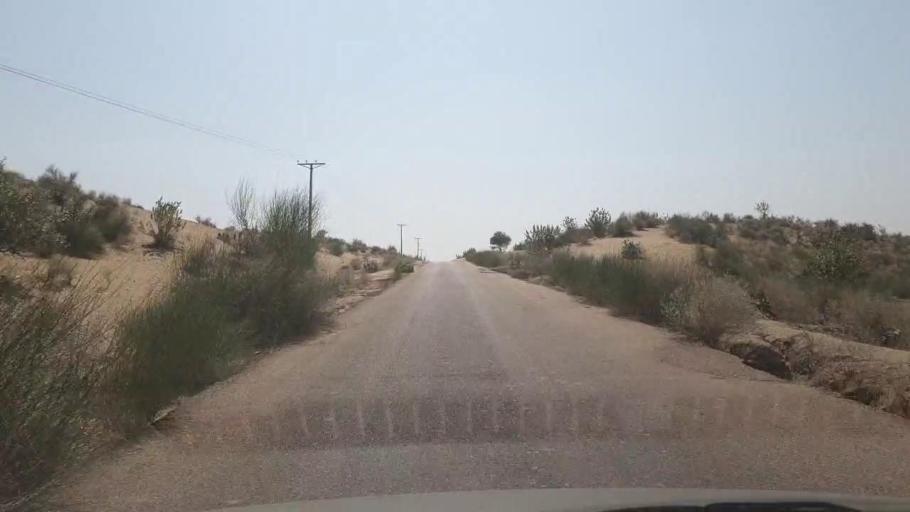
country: PK
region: Sindh
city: Chor
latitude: 25.6325
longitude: 70.1736
